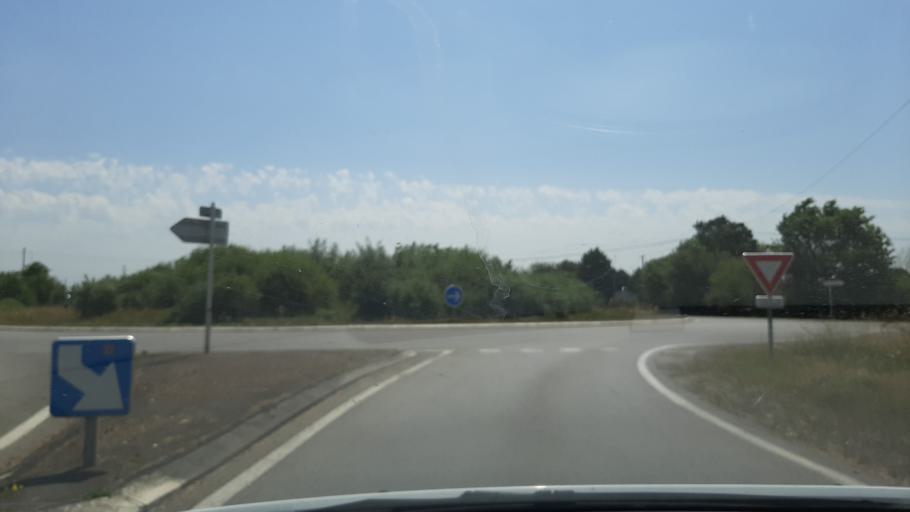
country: FR
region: Pays de la Loire
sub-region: Departement de la Vendee
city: Mouilleron-le-Captif
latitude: 46.7441
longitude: -1.4473
